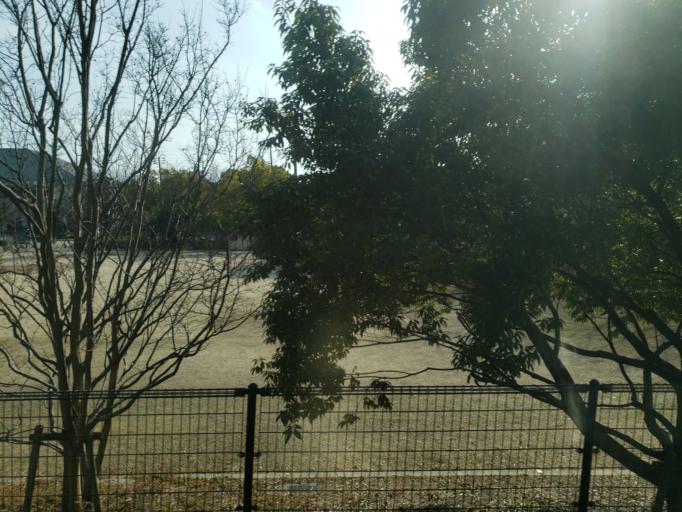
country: JP
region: Hyogo
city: Amagasaki
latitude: 34.7331
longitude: 135.4233
